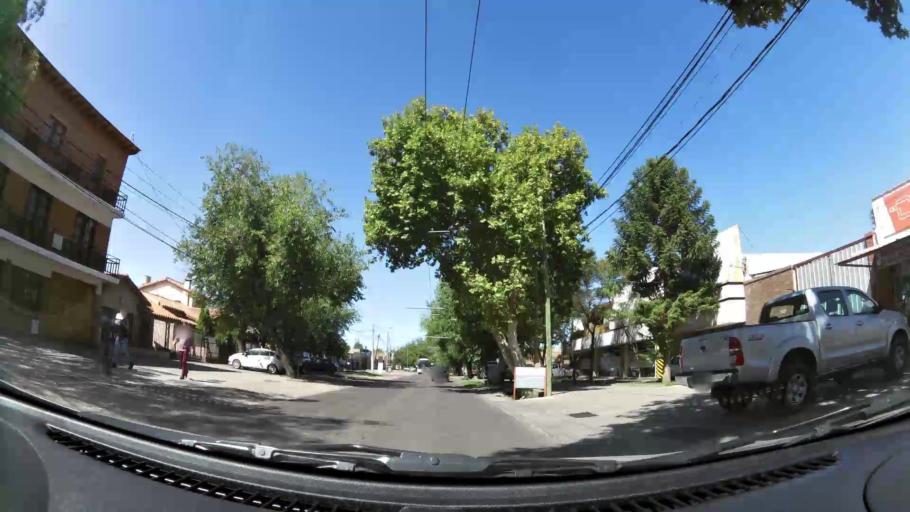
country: AR
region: Mendoza
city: Villa Nueva
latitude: -32.8934
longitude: -68.7932
